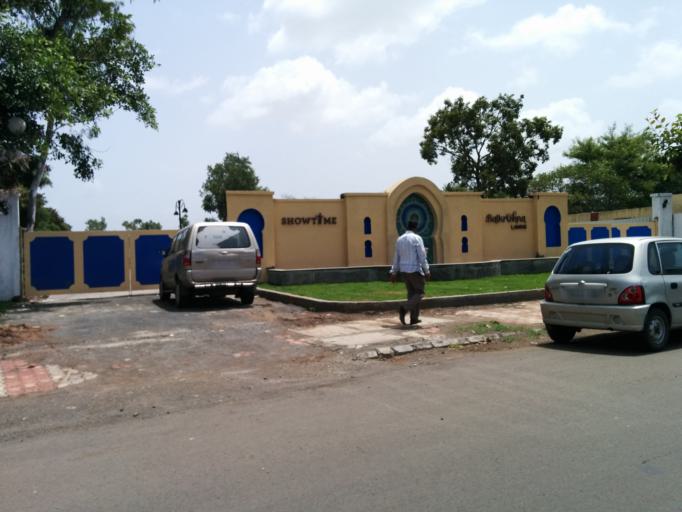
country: IN
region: Maharashtra
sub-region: Pune Division
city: Lohogaon
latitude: 18.5336
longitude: 73.9209
